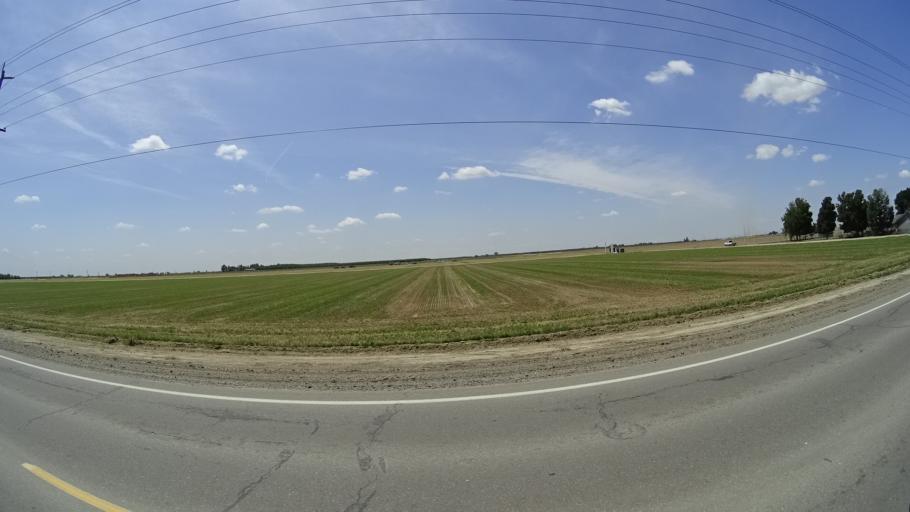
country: US
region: California
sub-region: Kings County
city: Home Garden
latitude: 36.2986
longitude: -119.5717
